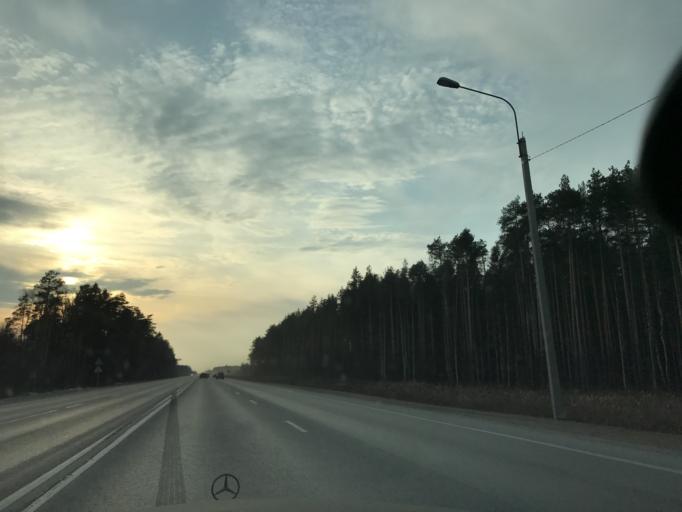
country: RU
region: Vladimir
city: Pokrov
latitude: 55.9245
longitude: 39.2670
